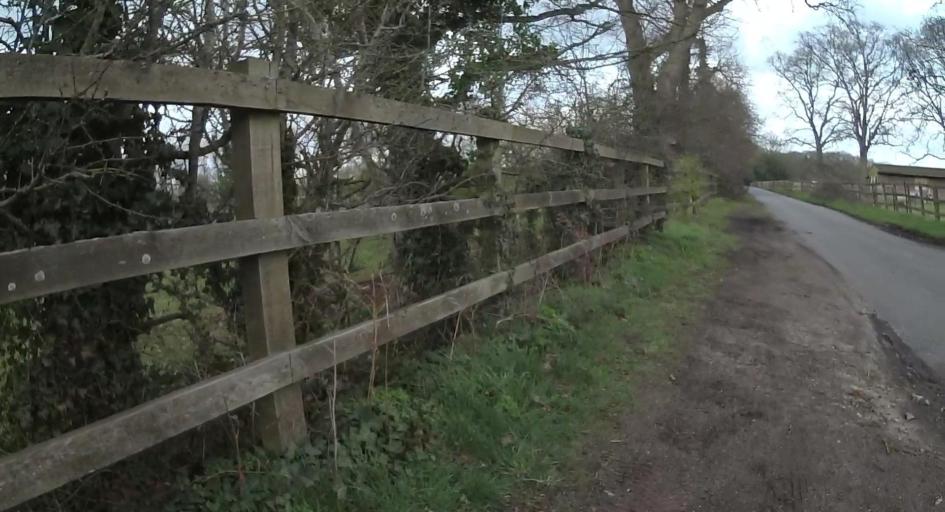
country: GB
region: England
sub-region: Surrey
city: Churt
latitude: 51.1434
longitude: -0.8024
